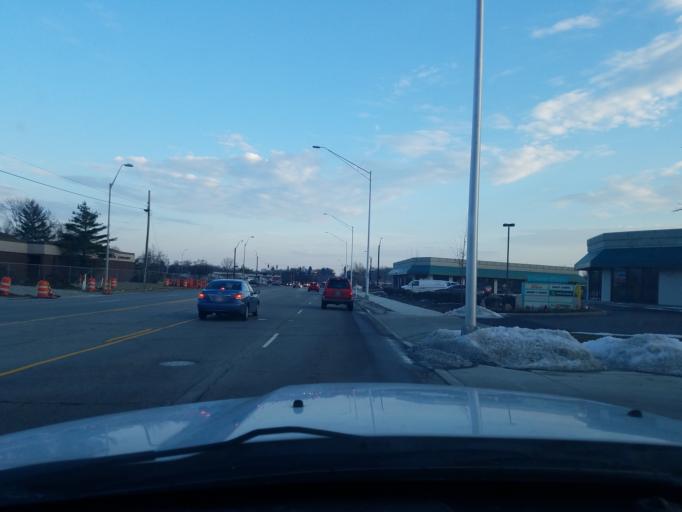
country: US
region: Ohio
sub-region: Montgomery County
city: Kettering
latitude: 39.6899
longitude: -84.1332
